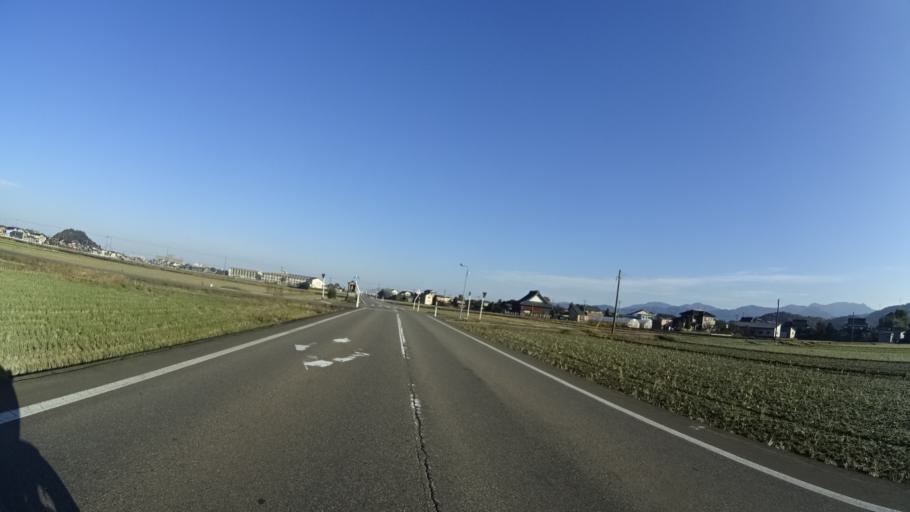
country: JP
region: Fukui
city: Fukui-shi
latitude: 36.0679
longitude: 136.2570
